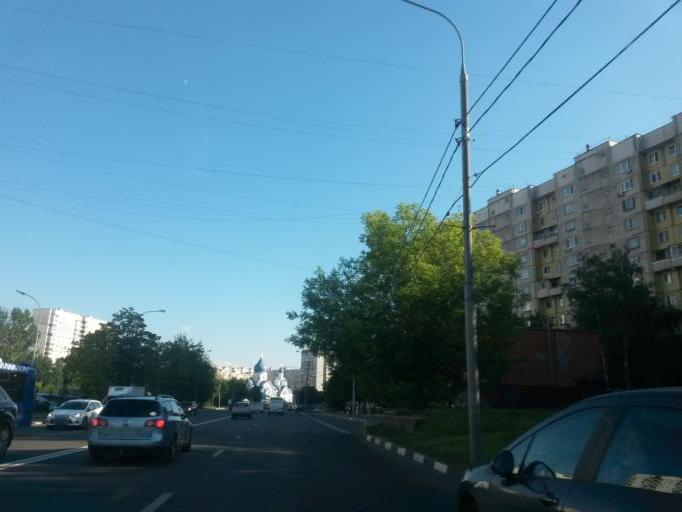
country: RU
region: Moscow
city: Orekhovo-Borisovo
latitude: 55.6102
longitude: 37.7445
